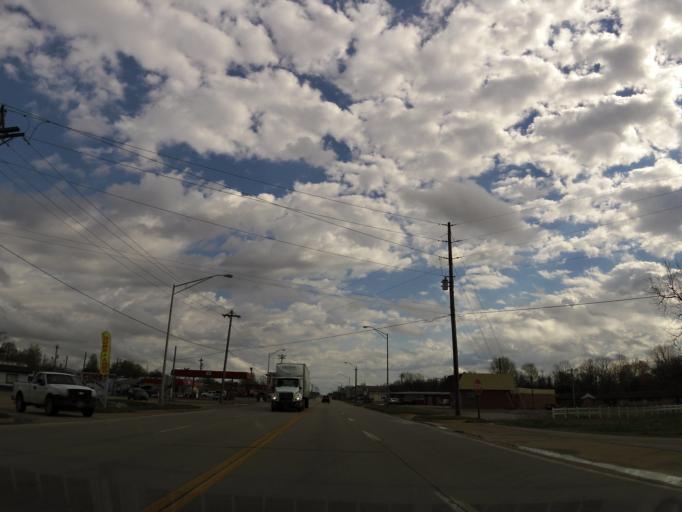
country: US
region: Missouri
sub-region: Butler County
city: Poplar Bluff
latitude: 36.7575
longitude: -90.3848
